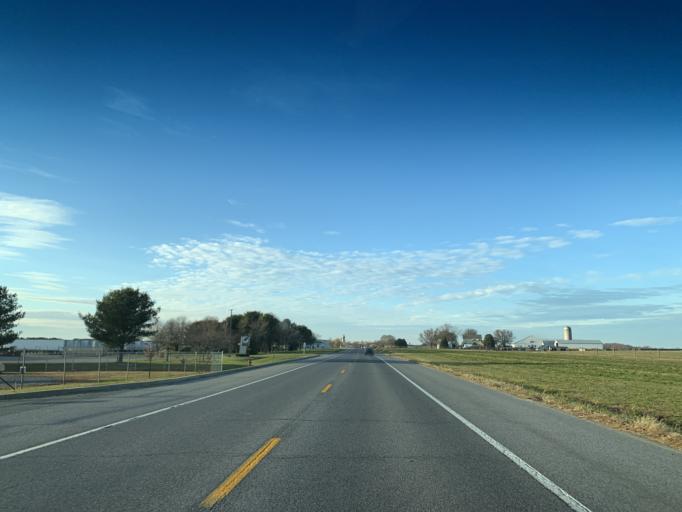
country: US
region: Maryland
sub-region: Kent County
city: Chestertown
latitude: 39.2570
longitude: -76.0822
